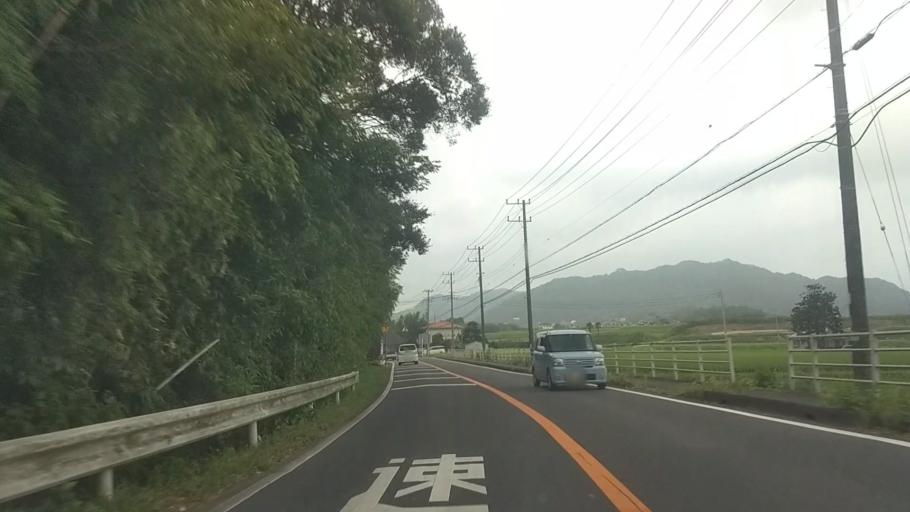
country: JP
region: Chiba
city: Kawaguchi
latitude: 35.1126
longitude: 140.0815
